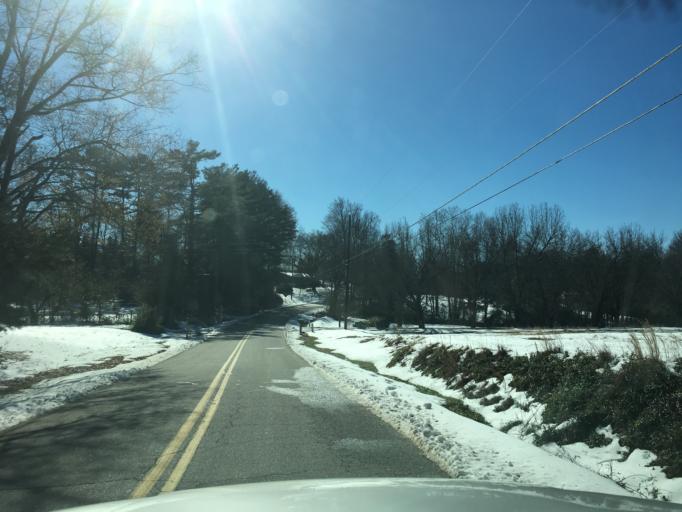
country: US
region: South Carolina
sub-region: Greenville County
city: Taylors
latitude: 34.9681
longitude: -82.3307
